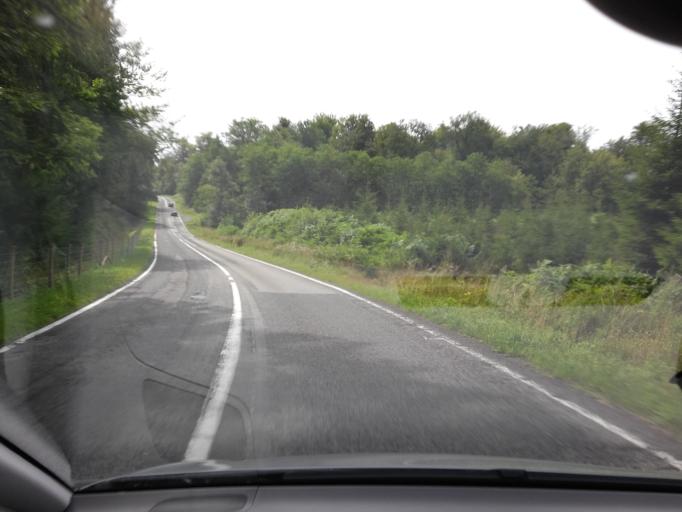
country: BE
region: Wallonia
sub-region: Province du Luxembourg
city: Chiny
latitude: 49.7785
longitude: 5.3485
